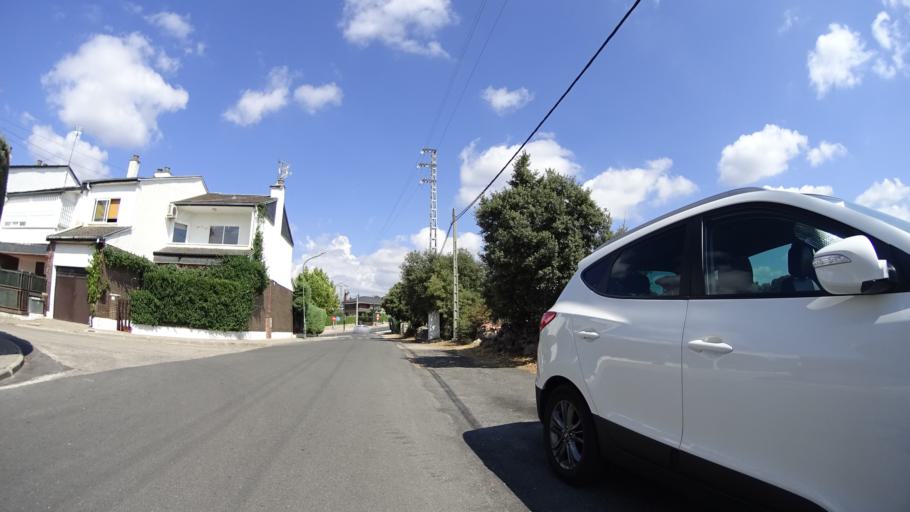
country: ES
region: Madrid
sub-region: Provincia de Madrid
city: Galapagar
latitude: 40.5838
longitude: -3.9943
